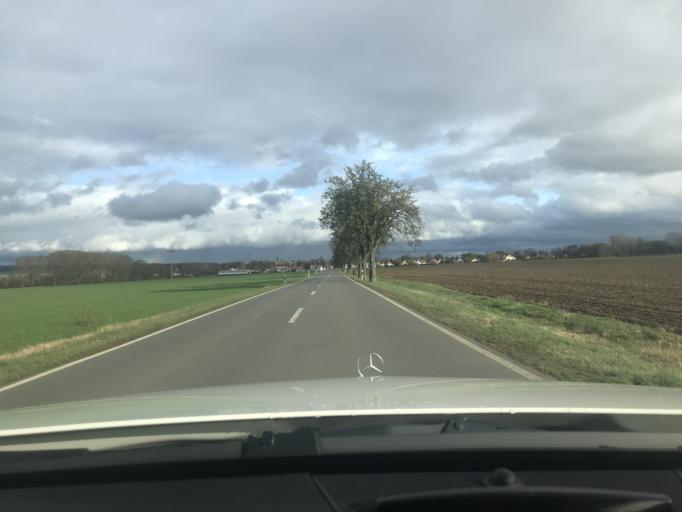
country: DE
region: Thuringia
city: Bufleben
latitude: 50.9990
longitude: 10.7240
